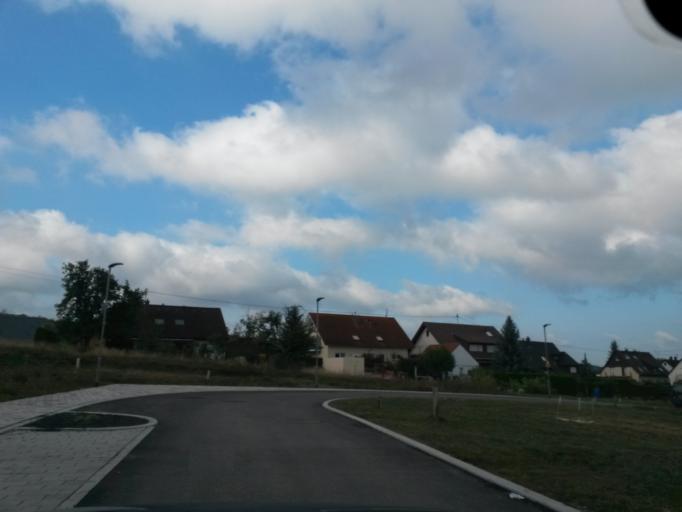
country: DE
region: Baden-Wuerttemberg
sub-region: Karlsruhe Region
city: Neuenburg
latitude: 48.8681
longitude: 8.5912
